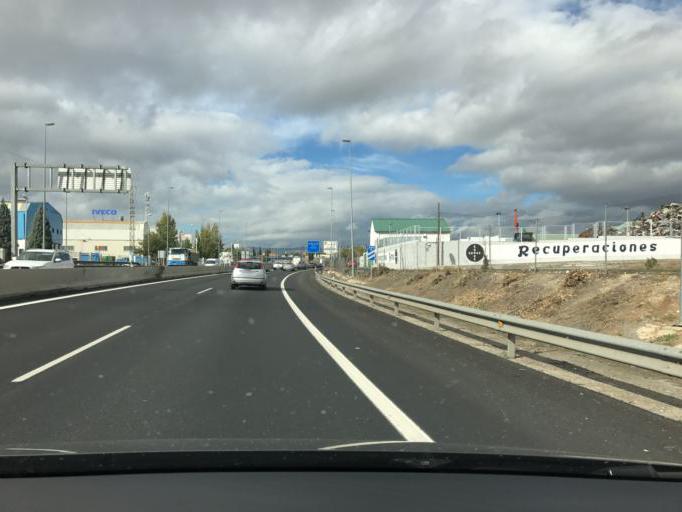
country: ES
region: Andalusia
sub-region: Provincia de Granada
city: Peligros
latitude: 37.2248
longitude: -3.6340
